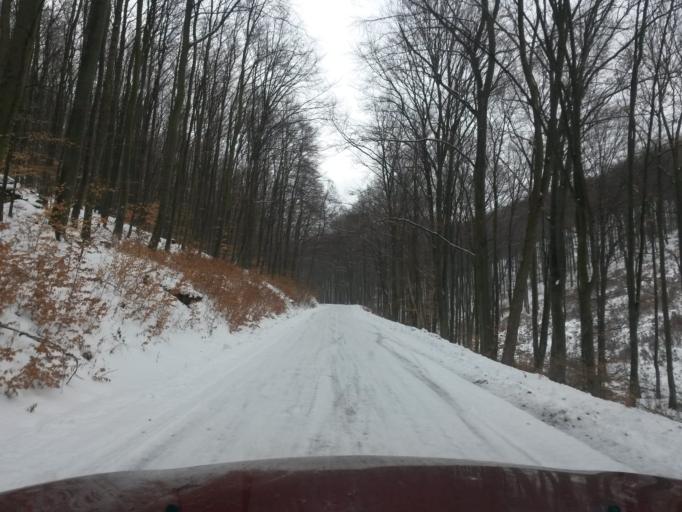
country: SK
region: Kosicky
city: Secovce
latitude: 48.8087
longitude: 21.5139
